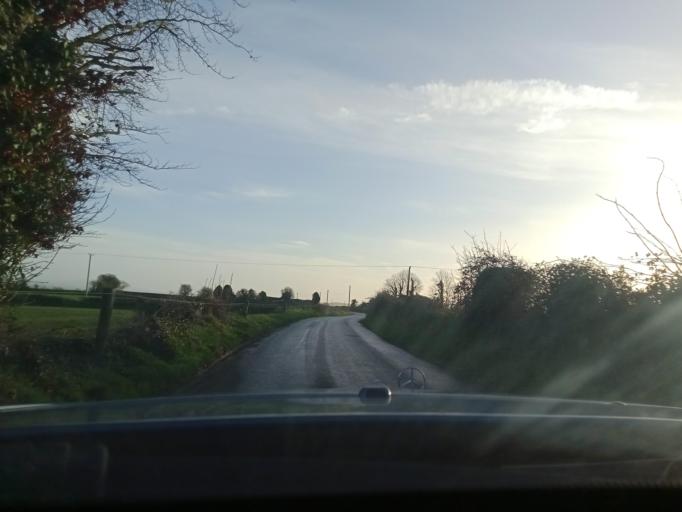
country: IE
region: Leinster
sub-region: Kilkenny
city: Callan
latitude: 52.4749
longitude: -7.4315
